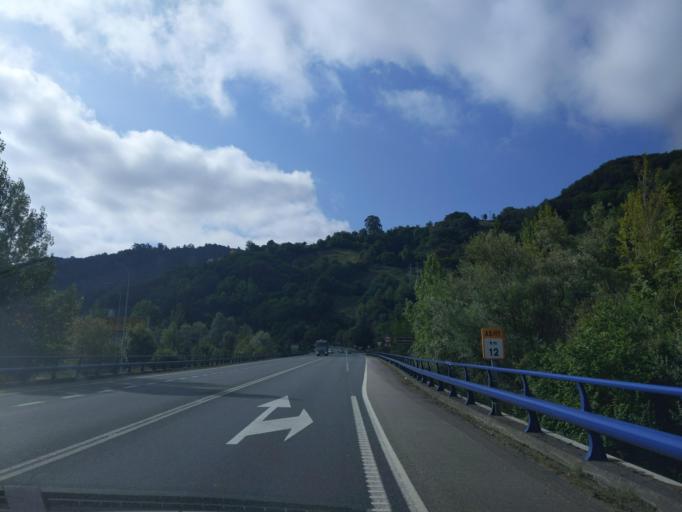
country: ES
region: Asturias
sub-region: Province of Asturias
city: El entrego
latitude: 43.2752
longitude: -5.6150
